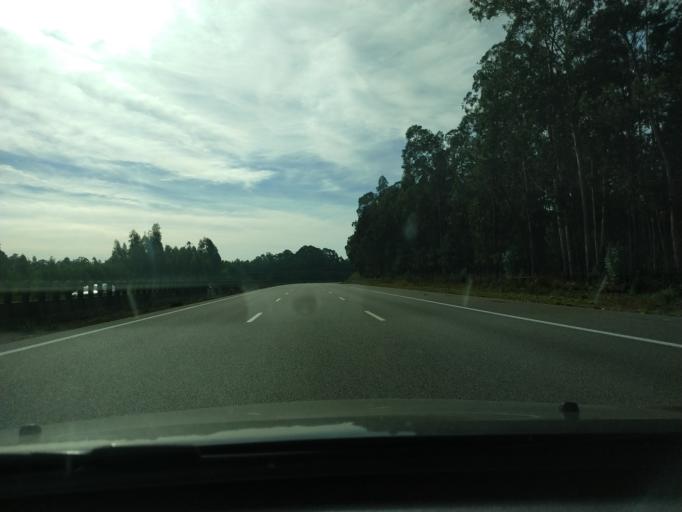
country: PT
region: Aveiro
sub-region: Ovar
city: Valega
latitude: 40.8605
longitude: -8.5569
